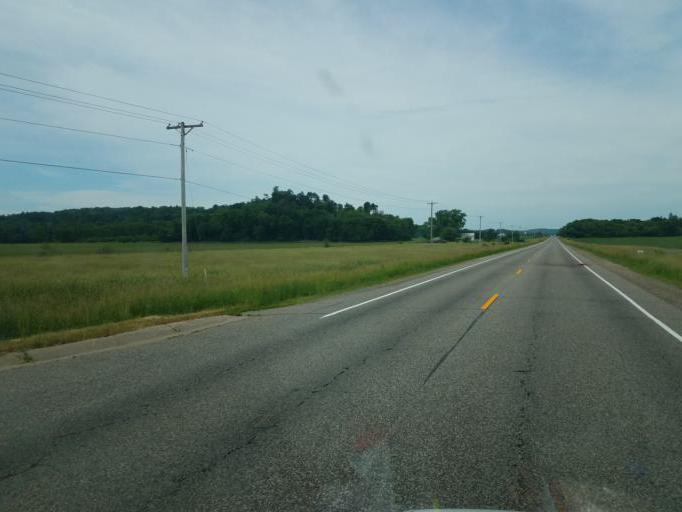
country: US
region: Wisconsin
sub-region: Juneau County
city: Mauston
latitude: 43.7890
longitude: -90.1118
